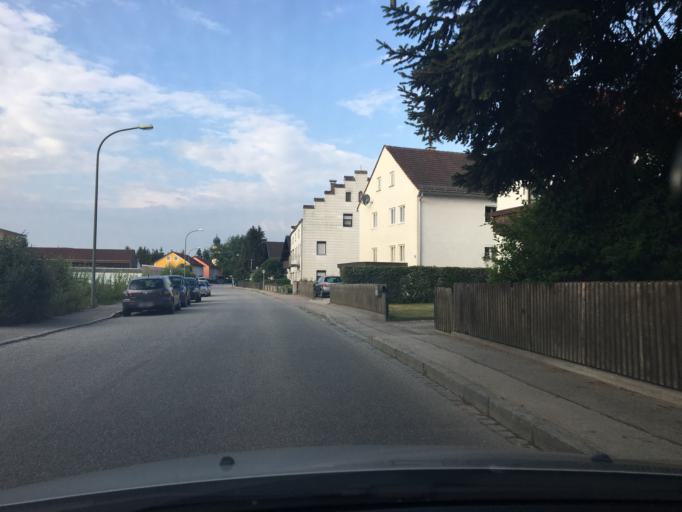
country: DE
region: Bavaria
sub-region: Lower Bavaria
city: Vilsbiburg
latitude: 48.4464
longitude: 12.3501
